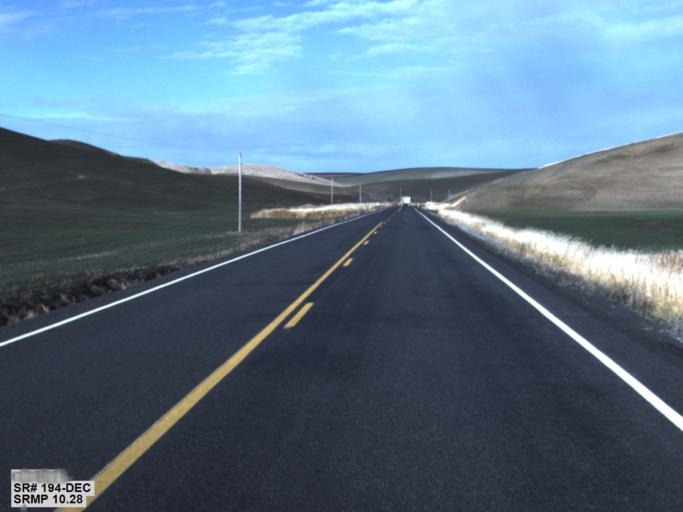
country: US
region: Washington
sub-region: Whitman County
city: Colfax
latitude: 46.7627
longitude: -117.3853
